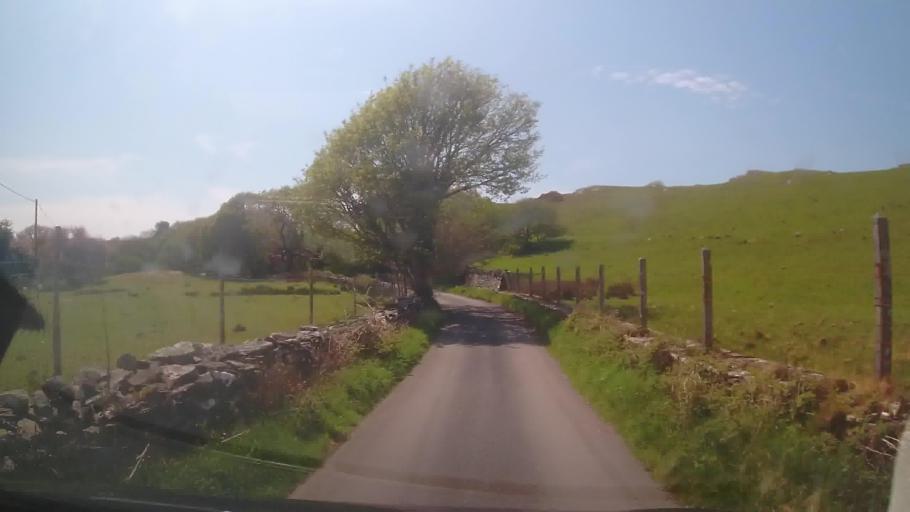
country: GB
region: Wales
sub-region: Gwynedd
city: Porthmadog
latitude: 52.9255
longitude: -4.1776
